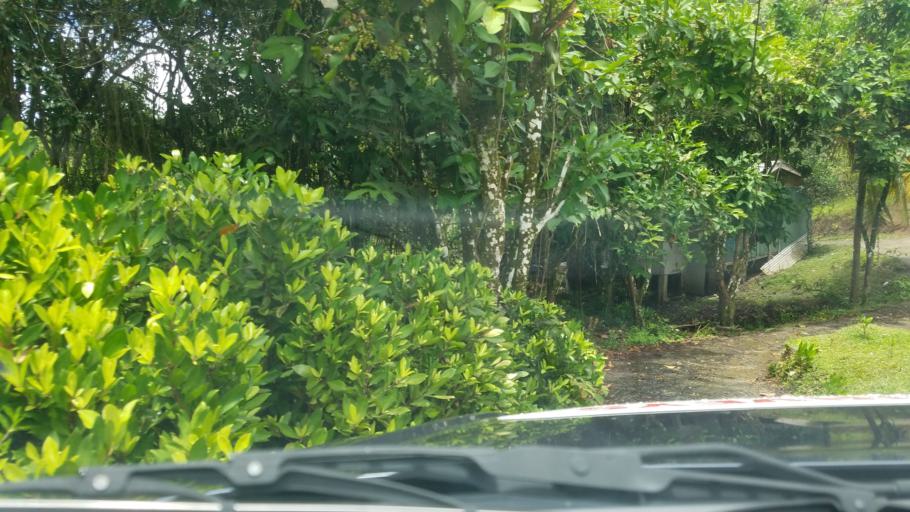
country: LC
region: Castries Quarter
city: Bisee
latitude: 13.9979
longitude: -60.9653
